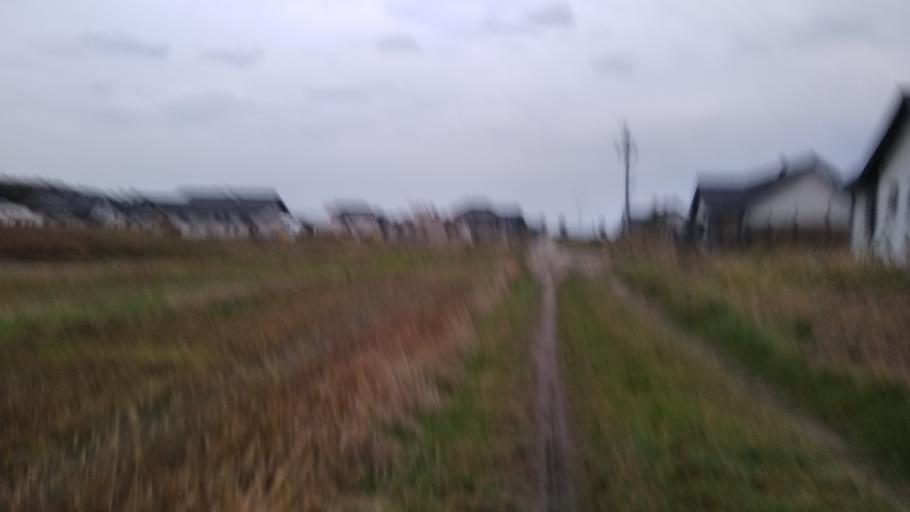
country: PL
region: Kujawsko-Pomorskie
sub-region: Powiat bydgoski
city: Osielsko
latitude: 53.2152
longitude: 18.1349
